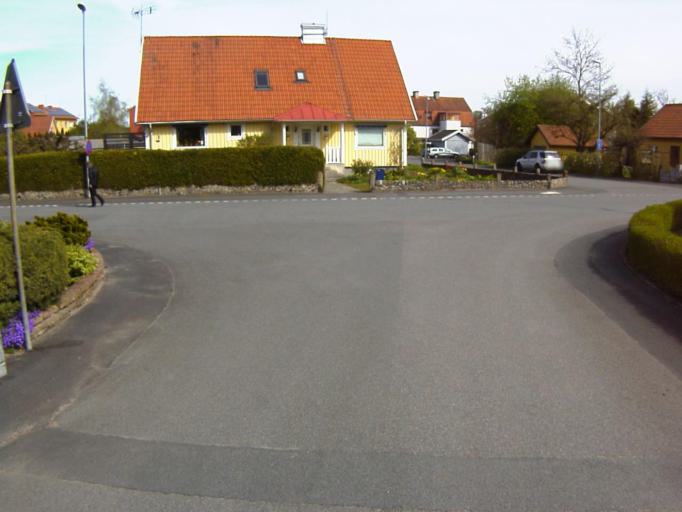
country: SE
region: Skane
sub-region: Kristianstads Kommun
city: Kristianstad
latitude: 56.0466
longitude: 14.1521
